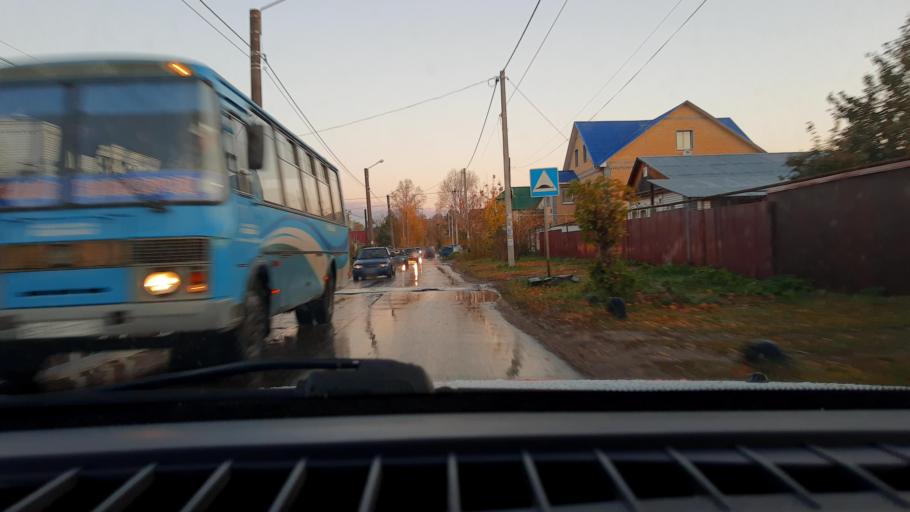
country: RU
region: Nizjnij Novgorod
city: Gorbatovka
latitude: 56.3328
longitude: 43.8311
